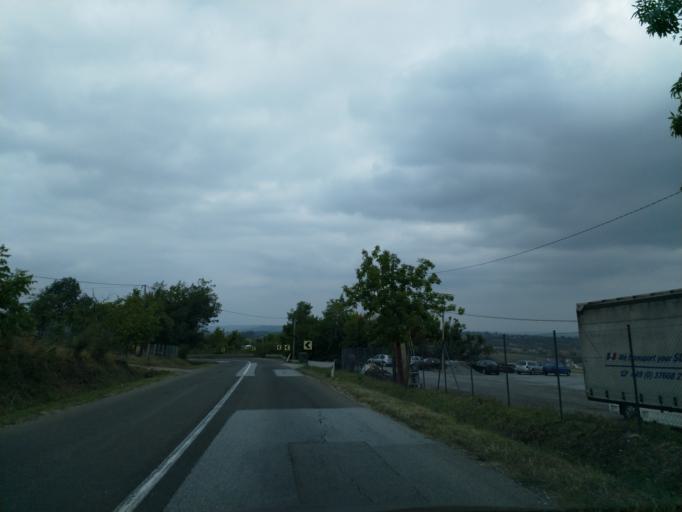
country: RS
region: Central Serbia
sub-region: Sumadijski Okrug
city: Topola
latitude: 44.1712
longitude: 20.7408
